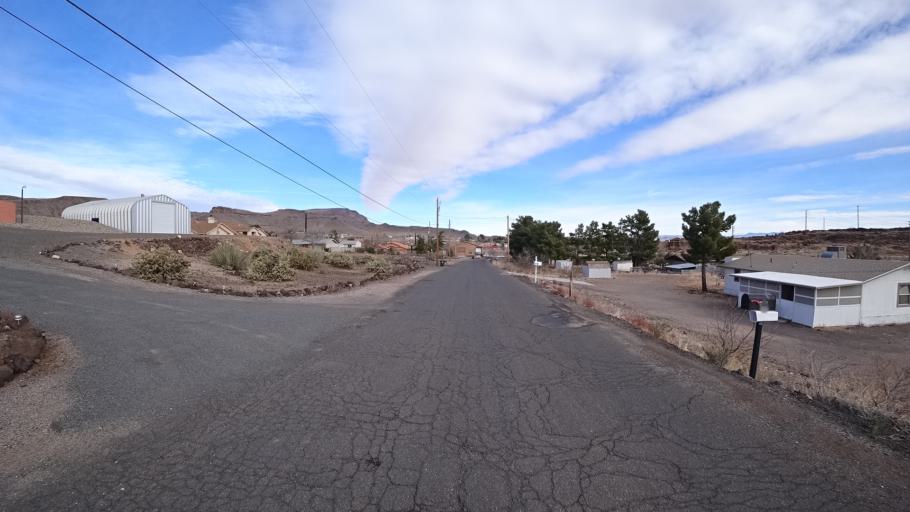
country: US
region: Arizona
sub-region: Mohave County
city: Kingman
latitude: 35.2283
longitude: -114.0484
